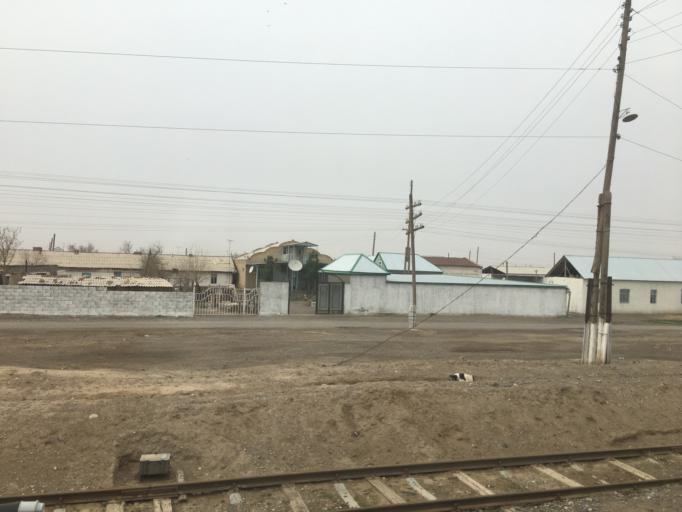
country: TM
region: Mary
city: Serhetabat
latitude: 35.6507
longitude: 62.5573
